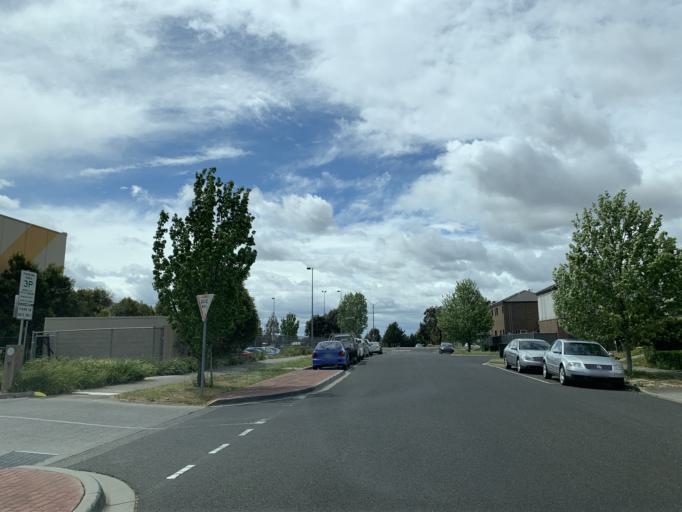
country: AU
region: Victoria
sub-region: Brimbank
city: Cairnlea
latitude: -37.7593
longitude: 144.7894
